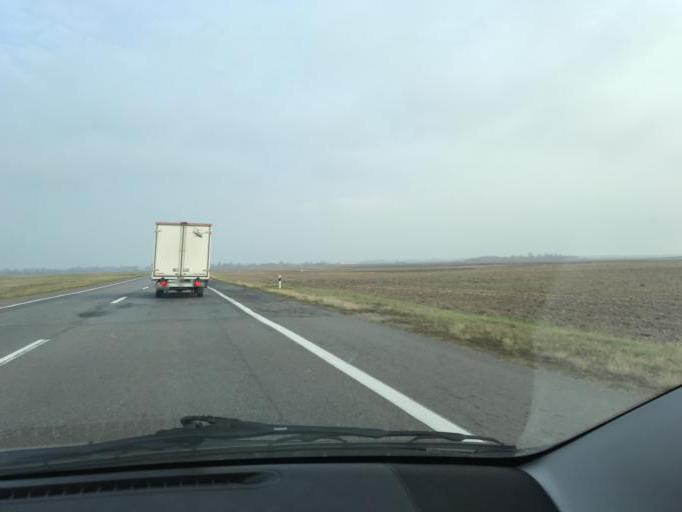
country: BY
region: Vitebsk
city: Syanno
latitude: 55.0975
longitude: 29.6634
